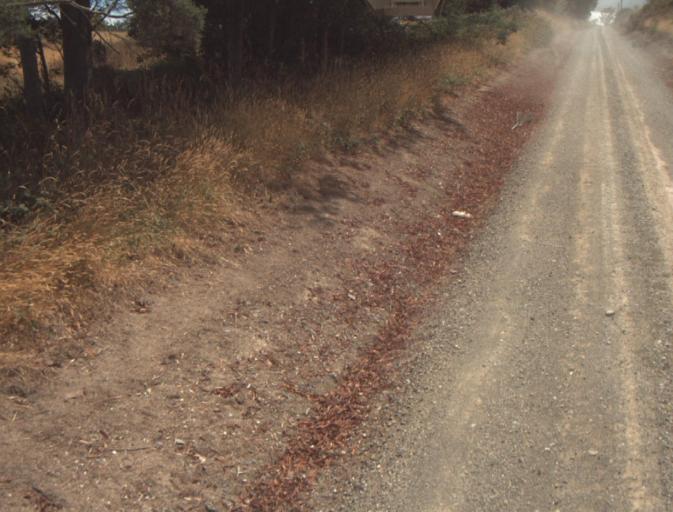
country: AU
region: Tasmania
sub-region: Launceston
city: Mayfield
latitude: -41.1955
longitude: 147.1700
